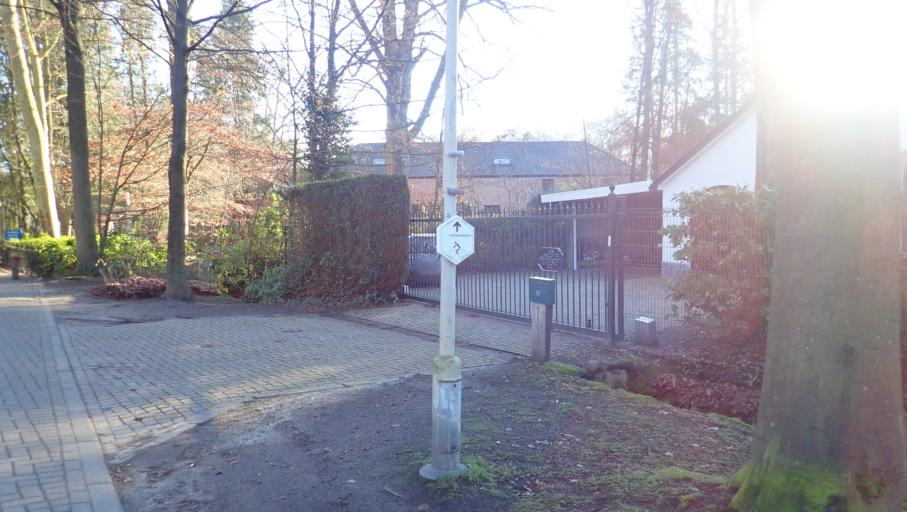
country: BE
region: Flanders
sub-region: Provincie Antwerpen
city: Schilde
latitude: 51.2507
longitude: 4.6262
